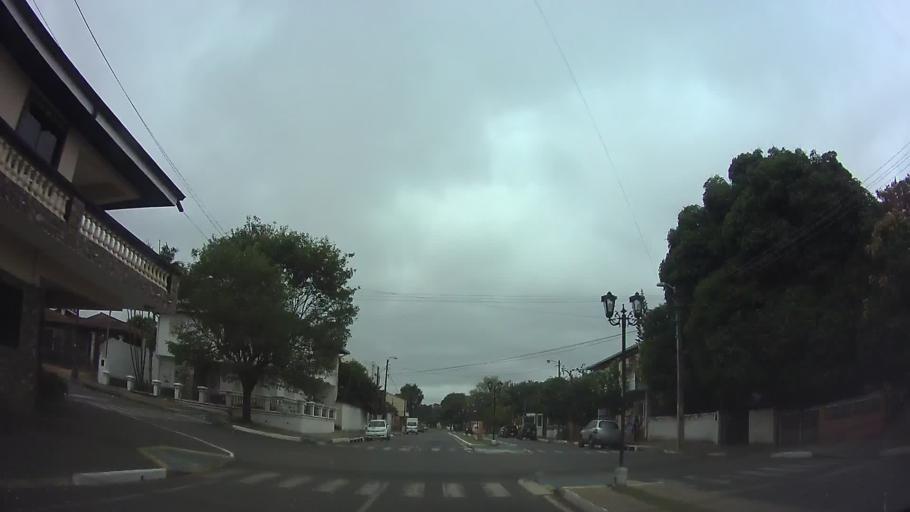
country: PY
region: Asuncion
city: Asuncion
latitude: -25.3089
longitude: -57.6267
